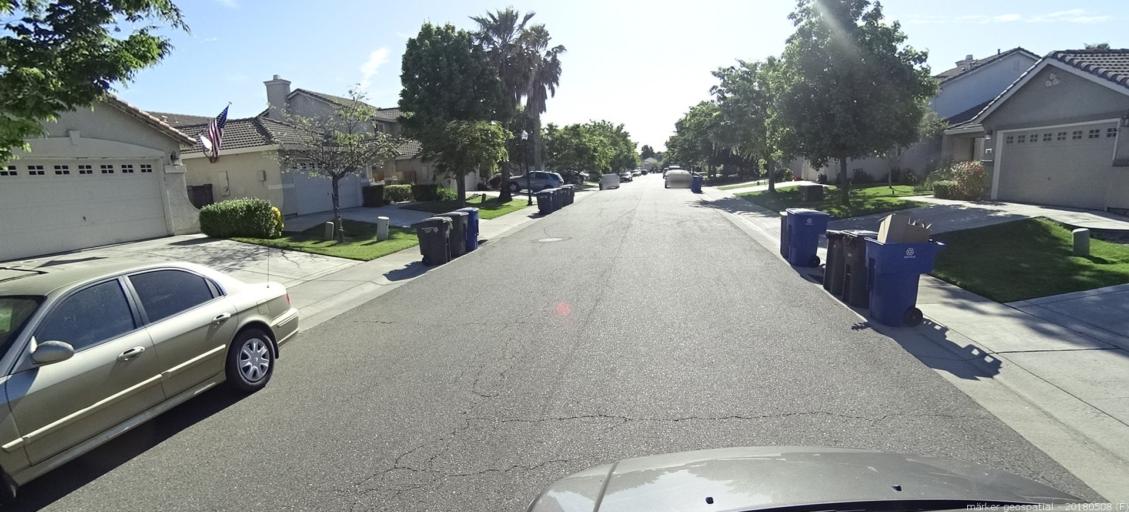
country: US
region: California
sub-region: Sacramento County
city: Elverta
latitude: 38.6779
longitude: -121.5067
